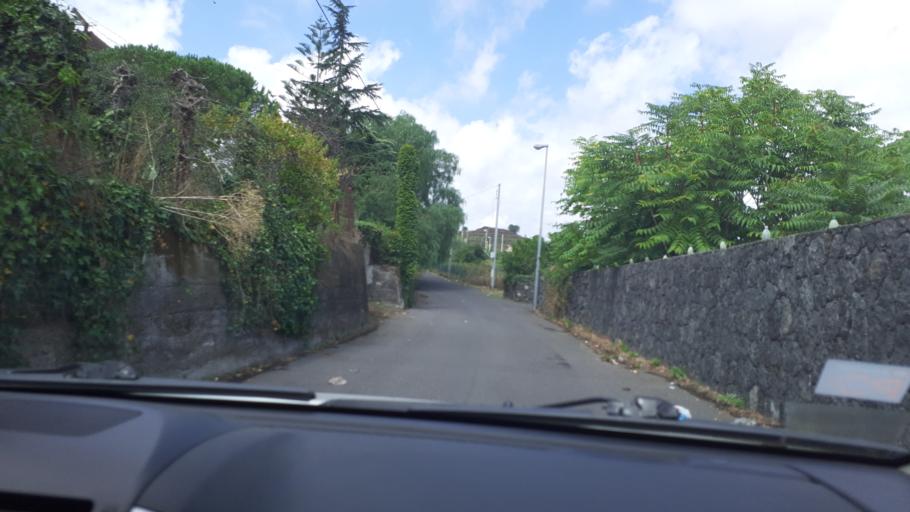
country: IT
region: Sicily
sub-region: Catania
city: Trecastagni
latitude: 37.5944
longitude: 15.0802
